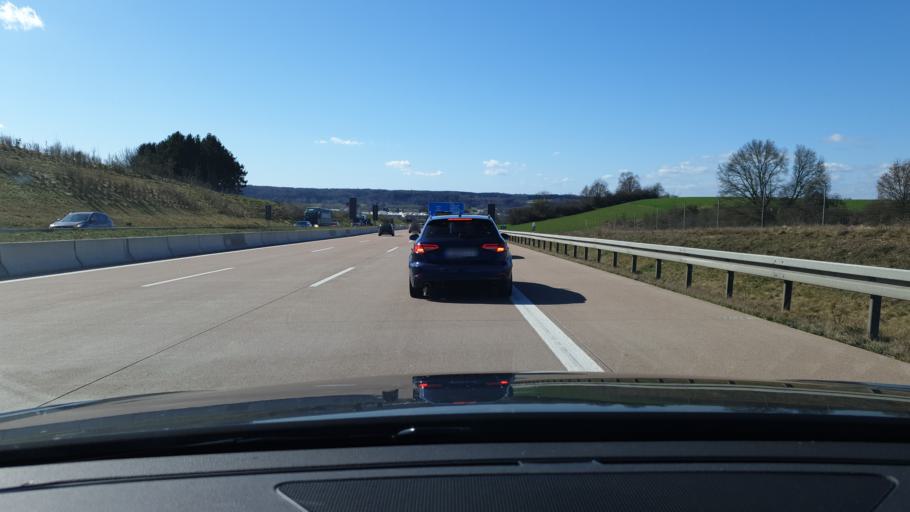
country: DE
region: Bavaria
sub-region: Swabia
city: Rofingen
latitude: 48.4127
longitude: 10.4552
